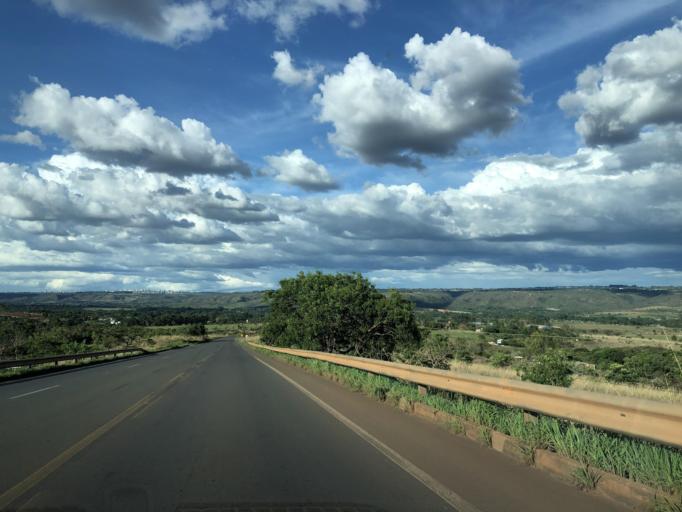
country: BR
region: Goias
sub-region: Luziania
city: Luziania
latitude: -16.0129
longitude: -48.1360
